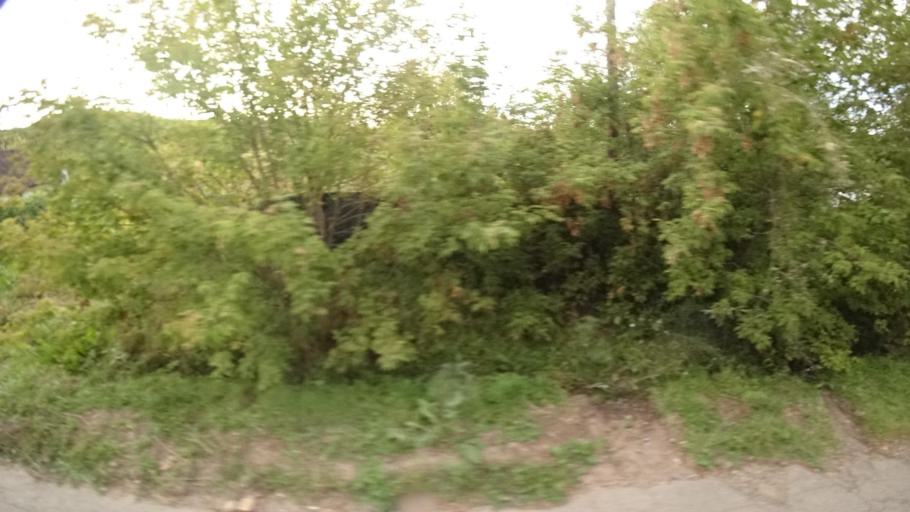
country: RU
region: Primorskiy
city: Yakovlevka
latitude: 44.4184
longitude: 133.4722
